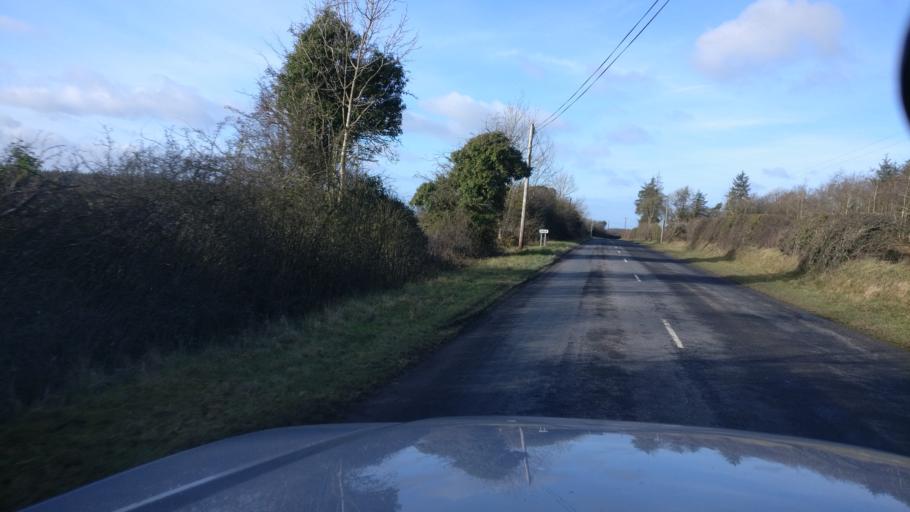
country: IE
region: Leinster
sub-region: Laois
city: Stradbally
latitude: 52.9277
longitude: -7.1964
